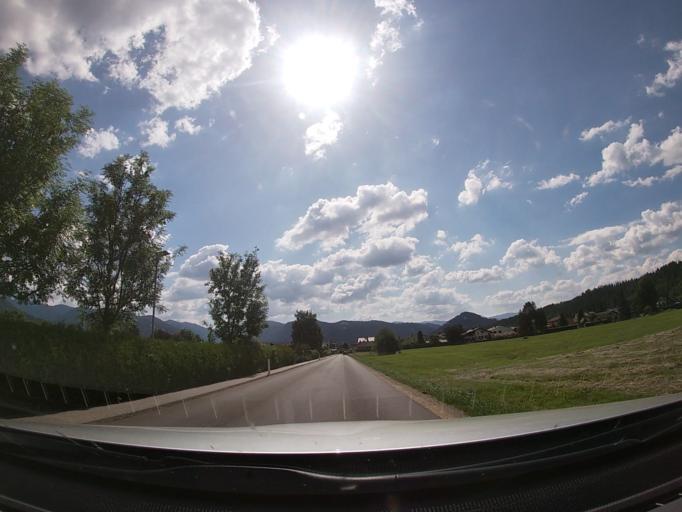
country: AT
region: Styria
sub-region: Politischer Bezirk Leoben
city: Trofaiach
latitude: 47.4266
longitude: 14.9830
